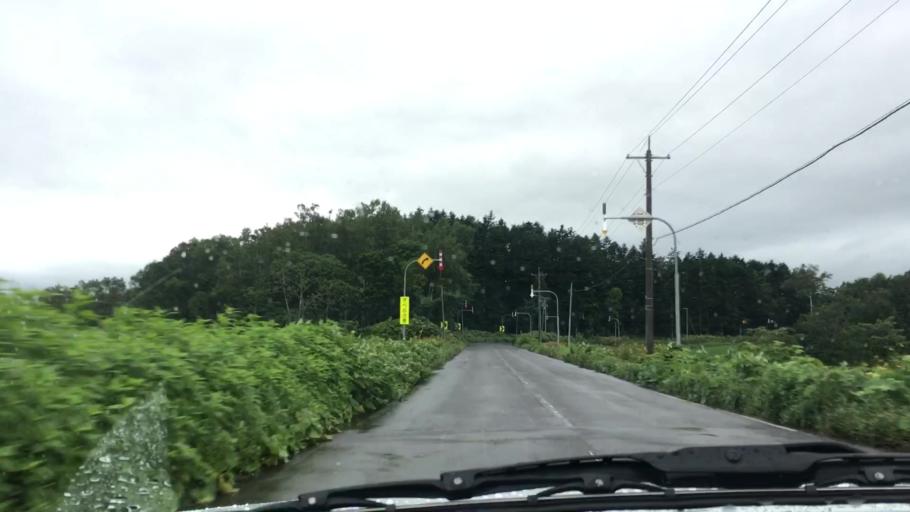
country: JP
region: Hokkaido
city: Niseko Town
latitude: 42.6853
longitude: 140.8229
